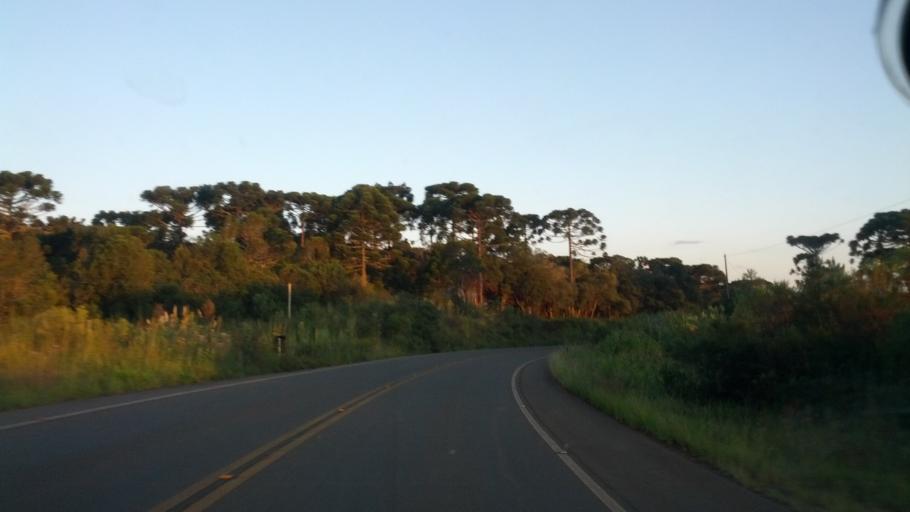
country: BR
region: Rio Grande do Sul
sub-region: Vacaria
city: Estrela
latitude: -27.8099
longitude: -50.8581
